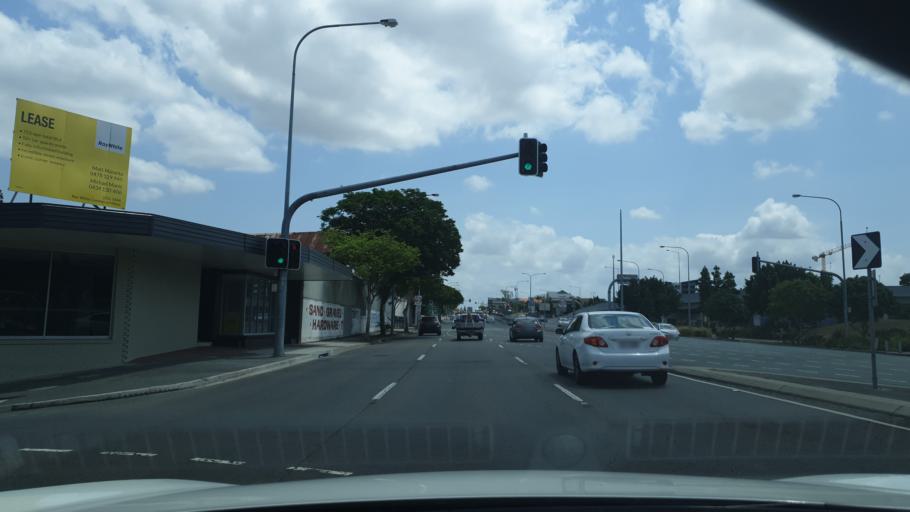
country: AU
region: Queensland
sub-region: Brisbane
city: Windsor
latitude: -27.4427
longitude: 153.0302
